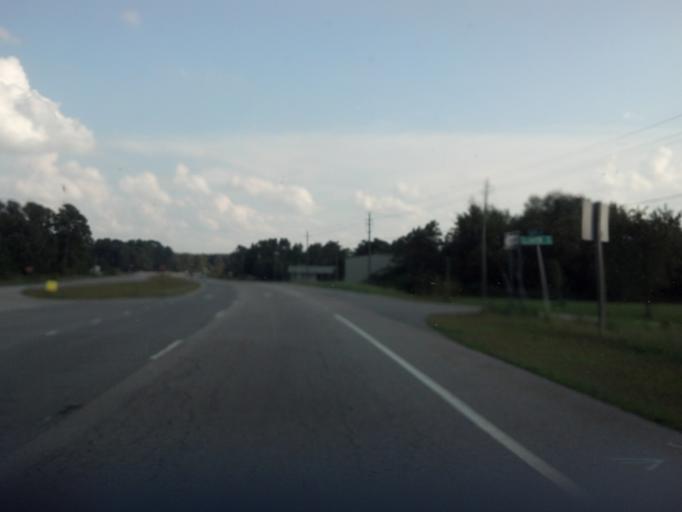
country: US
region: North Carolina
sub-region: Pitt County
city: Greenville
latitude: 35.6767
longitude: -77.3645
